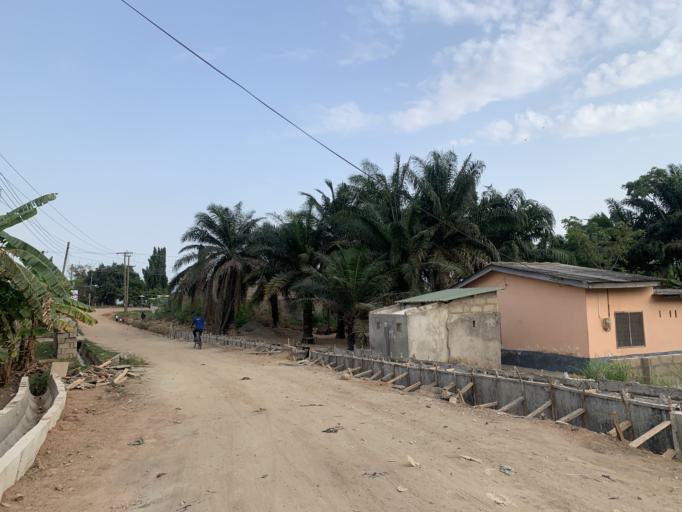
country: GH
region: Central
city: Winneba
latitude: 5.3563
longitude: -0.6258
